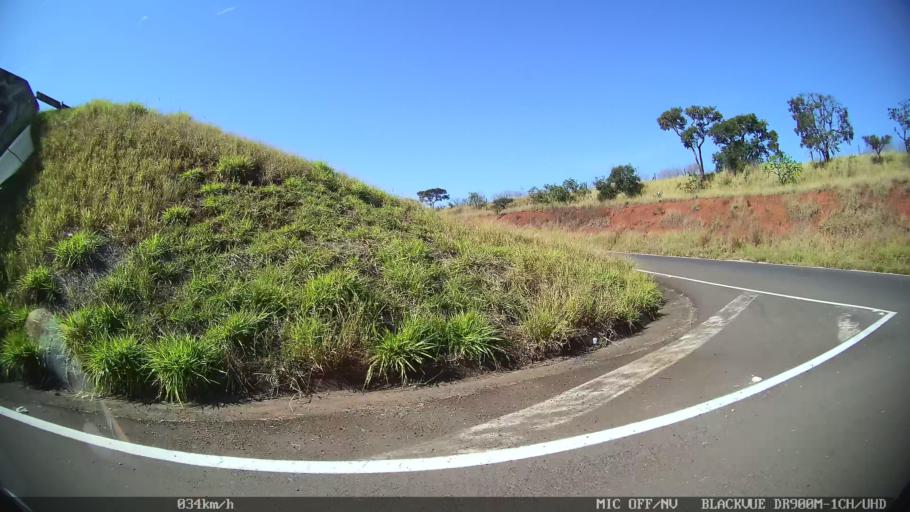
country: BR
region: Sao Paulo
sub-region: Batatais
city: Batatais
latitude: -20.9161
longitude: -47.5839
